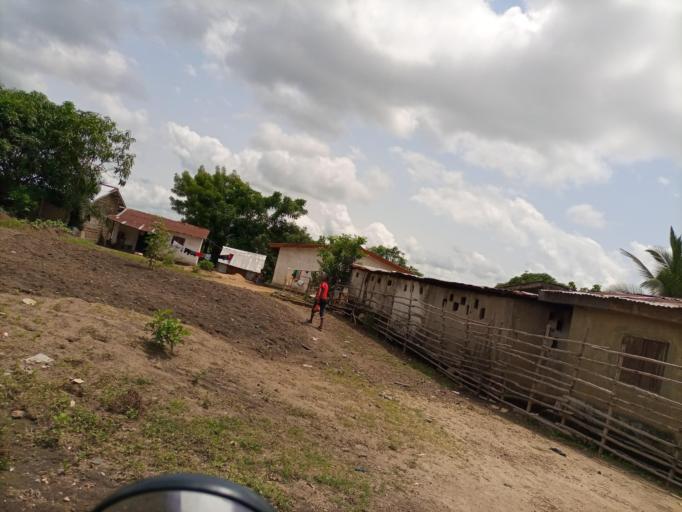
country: SL
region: Southern Province
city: Bo
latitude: 7.9771
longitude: -11.7648
